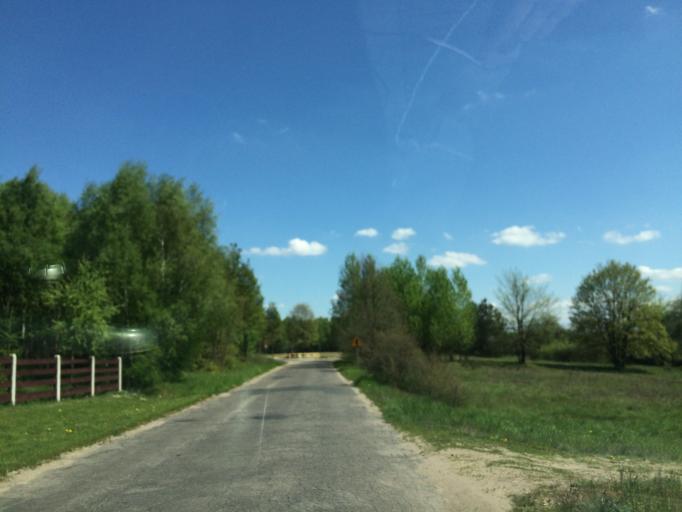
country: PL
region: Warmian-Masurian Voivodeship
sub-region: Powiat nowomiejski
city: Kurzetnik
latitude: 53.3847
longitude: 19.4756
